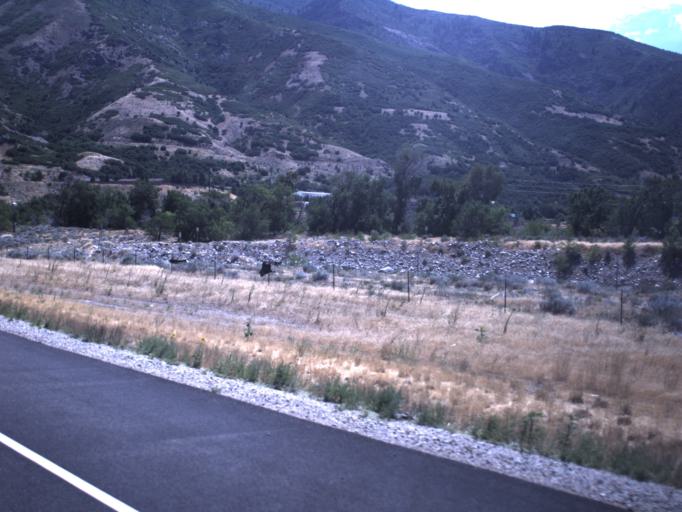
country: US
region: Utah
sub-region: Weber County
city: Uintah
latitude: 41.1371
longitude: -111.9068
